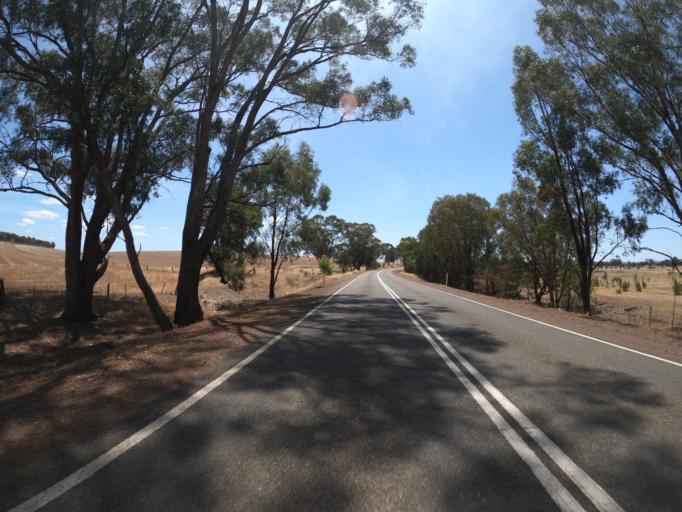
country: AU
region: Victoria
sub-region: Benalla
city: Benalla
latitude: -36.3244
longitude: 145.9592
